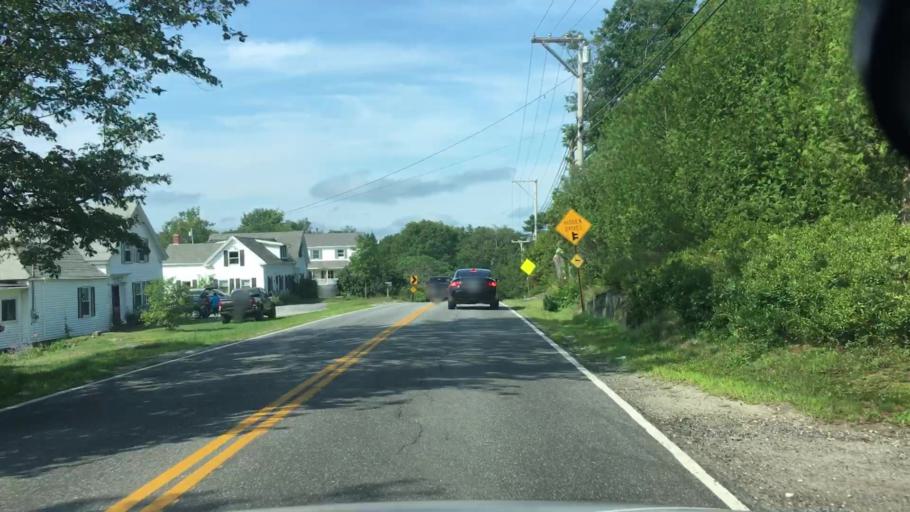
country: US
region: Maine
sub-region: Cumberland County
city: Harpswell Center
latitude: 43.7825
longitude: -69.9524
